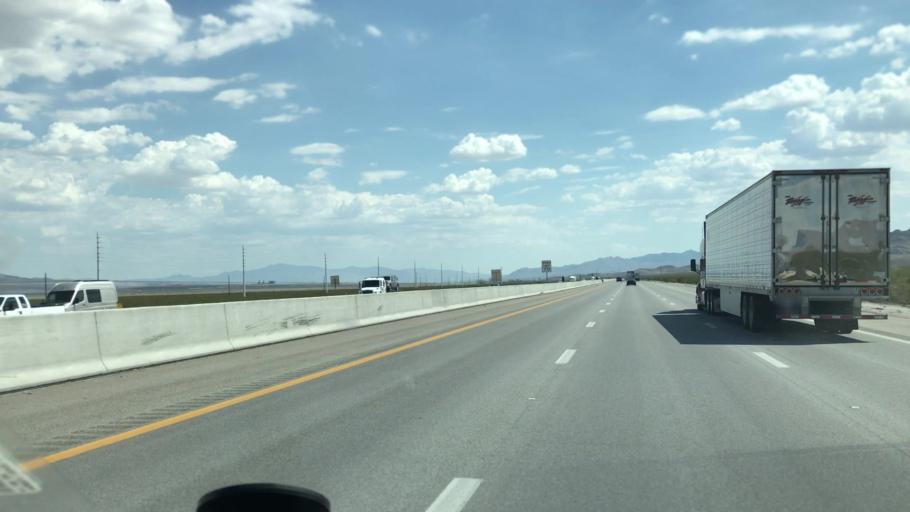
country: US
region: Nevada
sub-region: Clark County
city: Sandy Valley
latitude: 35.7003
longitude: -115.3705
